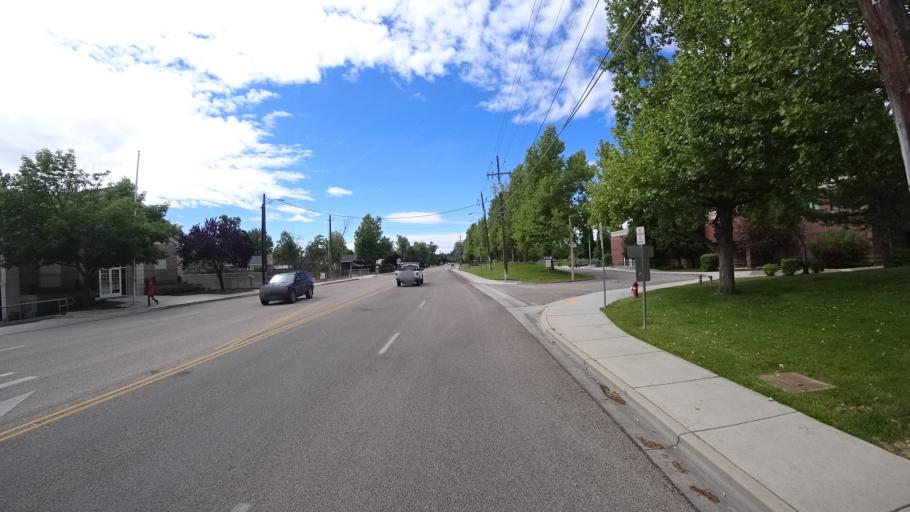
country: US
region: Idaho
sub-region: Ada County
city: Boise
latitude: 43.5780
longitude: -116.1734
